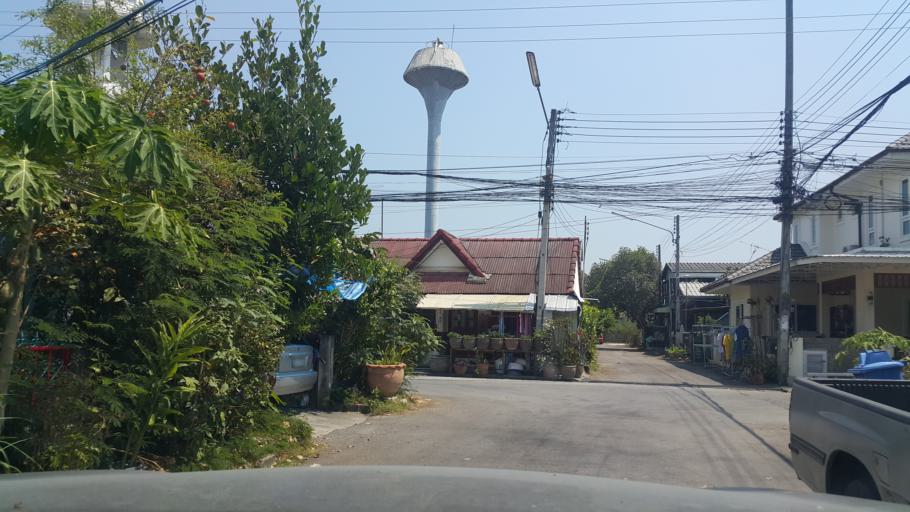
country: TH
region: Chiang Mai
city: San Kamphaeng
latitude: 18.7720
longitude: 99.0730
